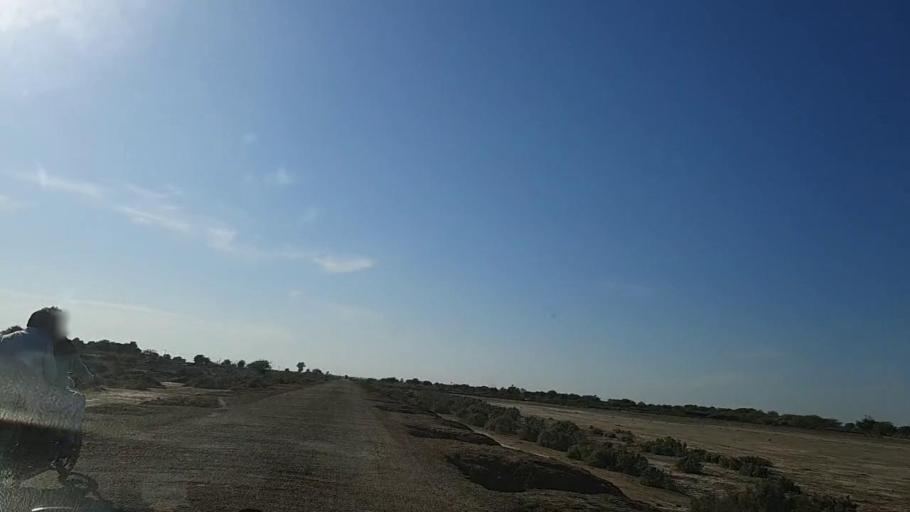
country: PK
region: Sindh
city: Pithoro
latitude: 25.5083
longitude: 69.4579
